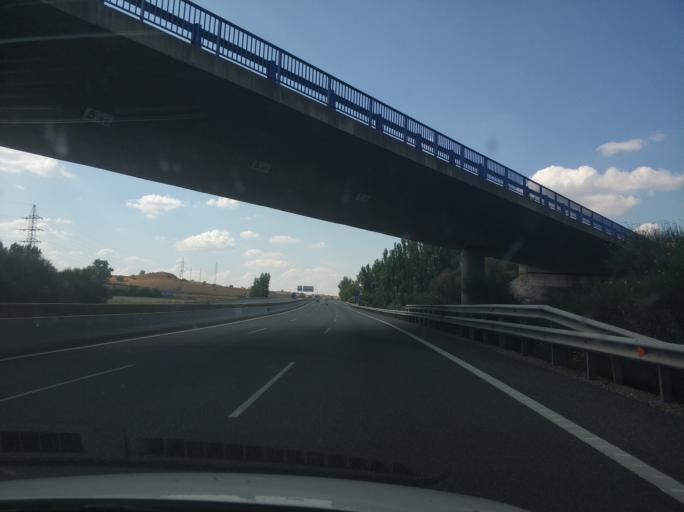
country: ES
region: Castille and Leon
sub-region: Provincia de Zamora
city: Benavente
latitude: 42.0165
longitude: -5.6660
